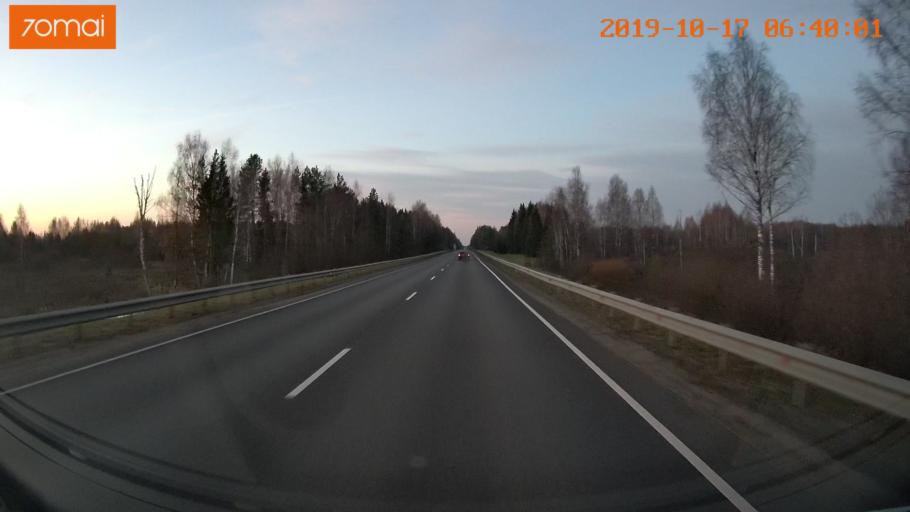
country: RU
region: Ivanovo
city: Novoye Leushino
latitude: 56.6351
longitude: 40.5735
